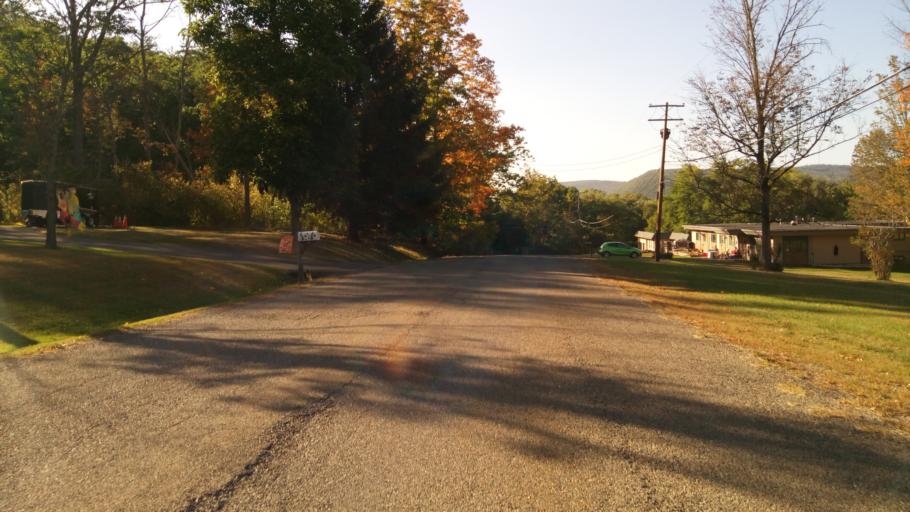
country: US
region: New York
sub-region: Chemung County
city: West Elmira
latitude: 42.0699
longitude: -76.8399
